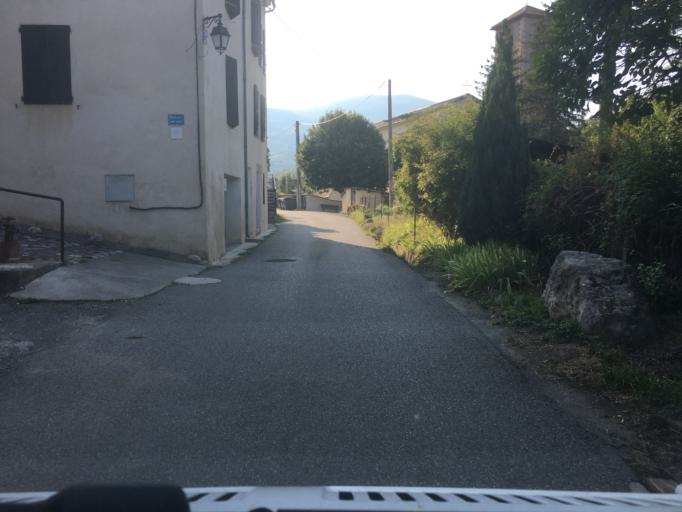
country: FR
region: Provence-Alpes-Cote d'Azur
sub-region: Departement des Alpes-de-Haute-Provence
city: Mallemoisson
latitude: 43.9418
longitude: 6.1730
